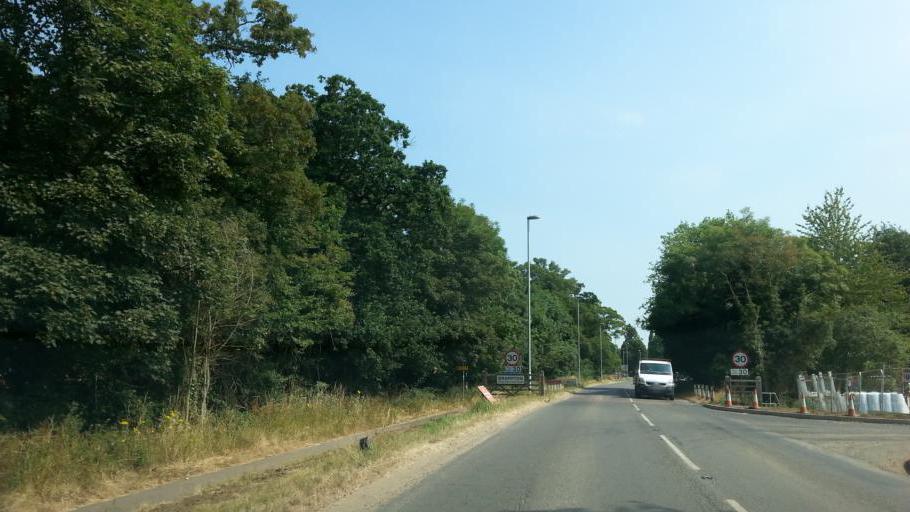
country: GB
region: England
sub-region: Cambridgeshire
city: Brampton
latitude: 52.3145
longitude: -0.2239
